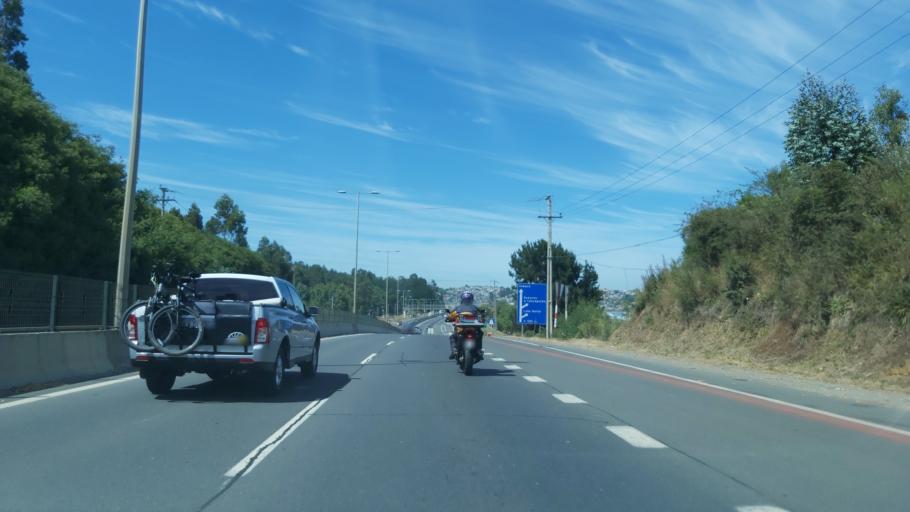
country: CL
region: Biobio
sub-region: Provincia de Concepcion
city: Coronel
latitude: -37.0594
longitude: -73.1401
